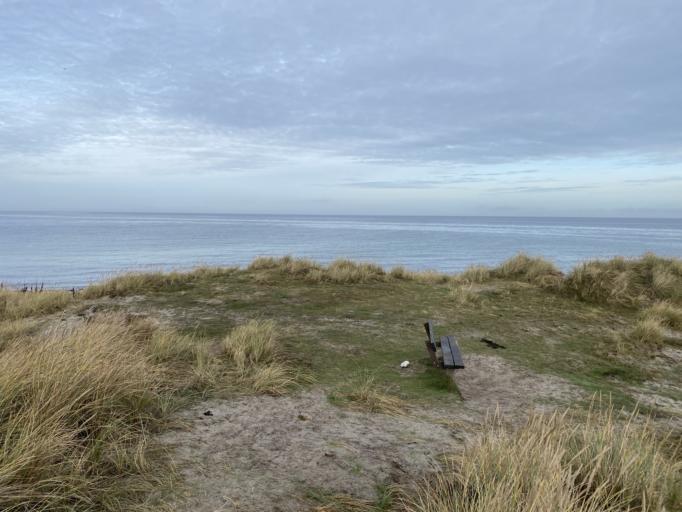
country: DK
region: Capital Region
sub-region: Halsnaes Kommune
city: Hundested
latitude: 55.9764
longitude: 11.7767
